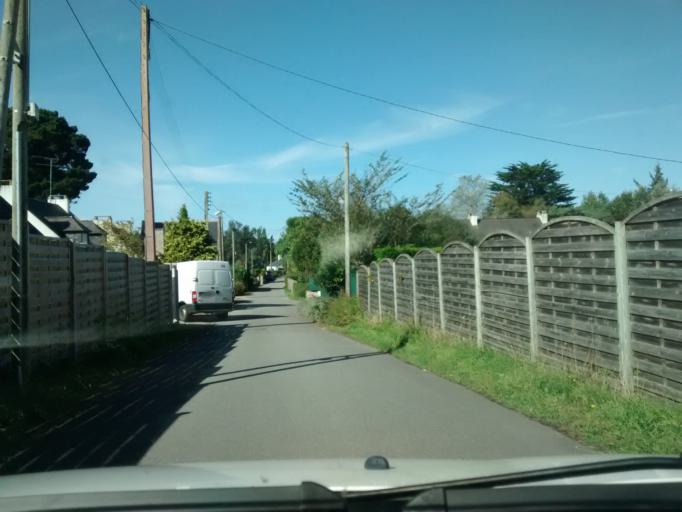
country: FR
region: Brittany
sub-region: Departement d'Ille-et-Vilaine
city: Saint-Briac-sur-Mer
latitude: 48.6287
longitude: -2.1363
